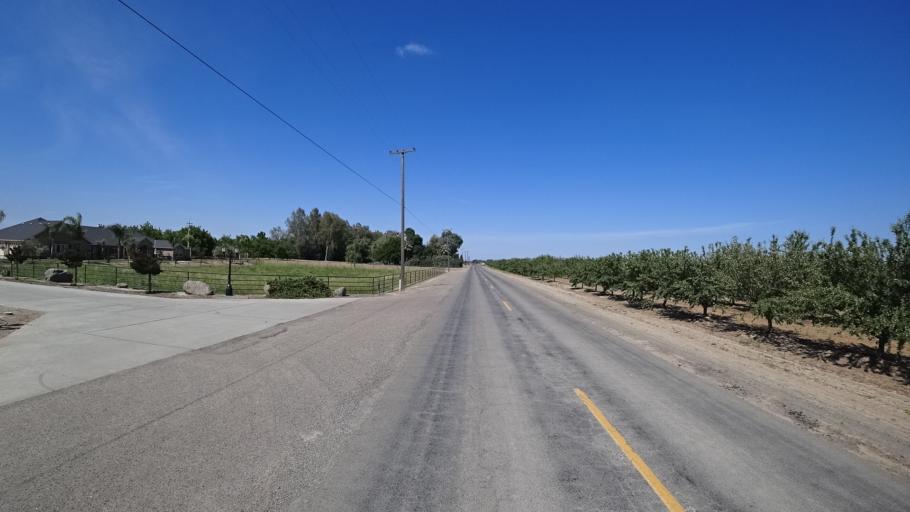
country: US
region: California
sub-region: Kings County
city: Armona
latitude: 36.2693
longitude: -119.7036
